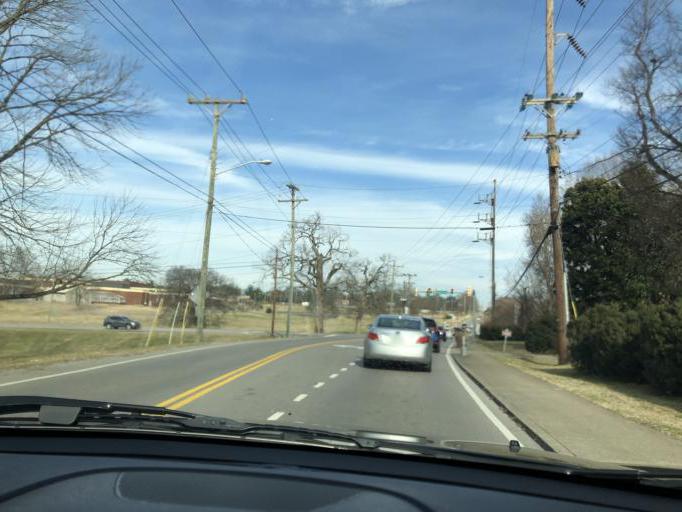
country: US
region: Tennessee
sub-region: Davidson County
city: Lakewood
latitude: 36.1826
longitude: -86.6777
